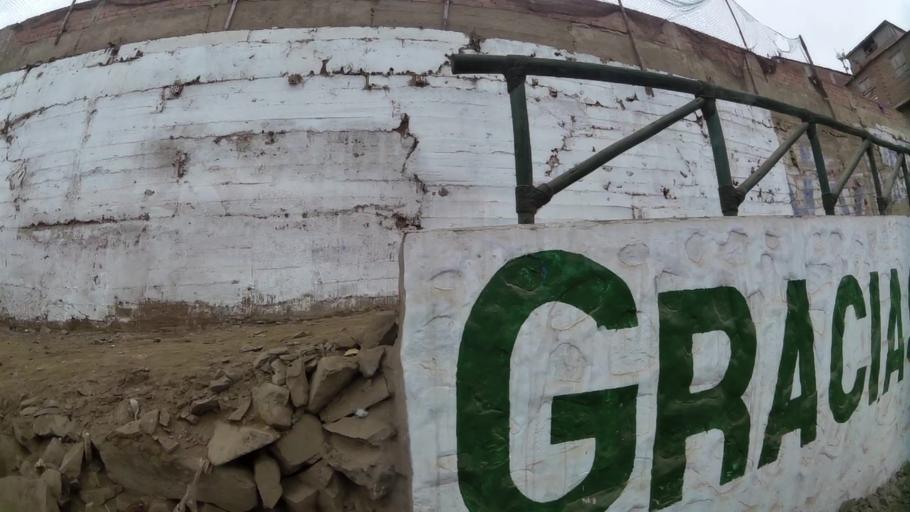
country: PE
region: Lima
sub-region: Lima
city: Surco
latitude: -12.1771
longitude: -76.9549
